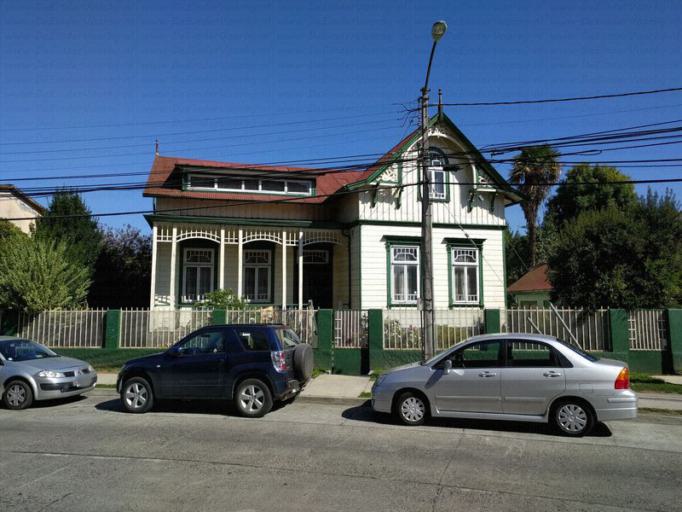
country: CL
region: Los Rios
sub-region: Provincia de Valdivia
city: Valdivia
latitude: -39.8170
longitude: -73.2431
